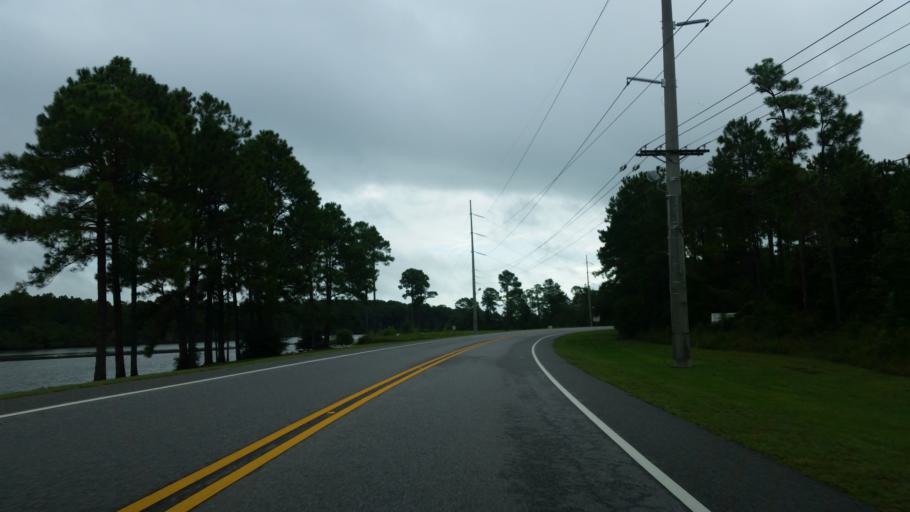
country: US
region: Alabama
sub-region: Baldwin County
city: Gulf Shores
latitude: 30.2864
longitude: -87.6442
